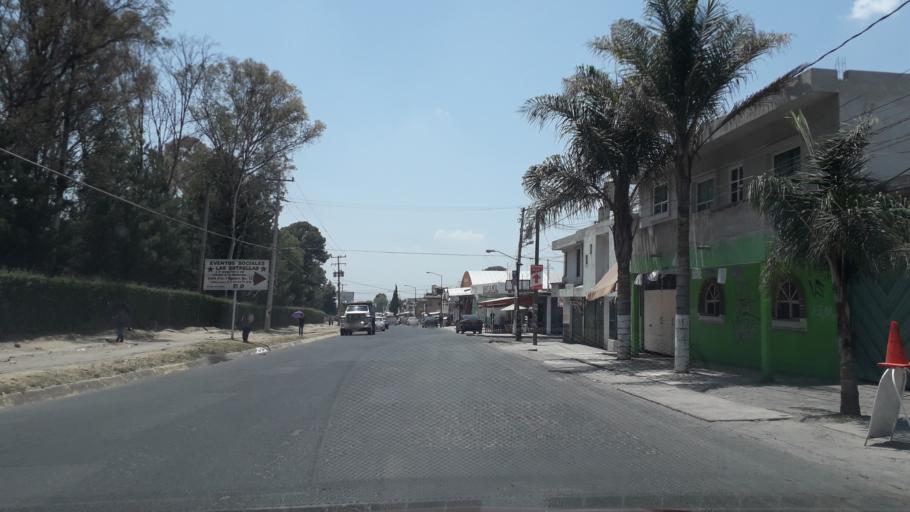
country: MX
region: Puebla
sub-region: Puebla
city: Santa Maria Xonacatepec
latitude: 19.0786
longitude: -98.1109
